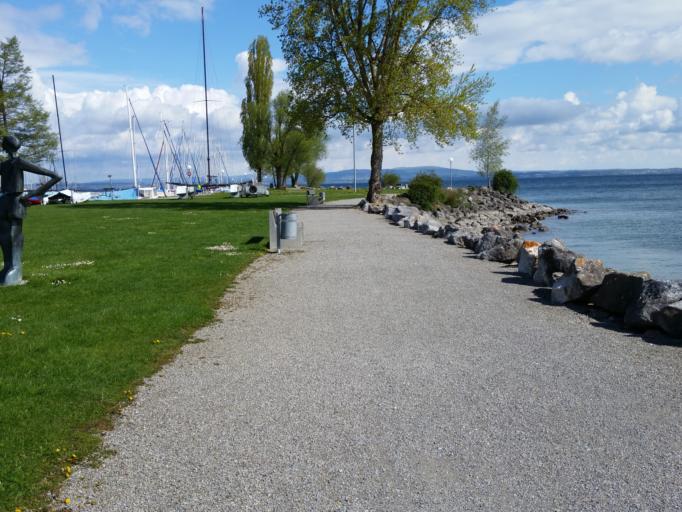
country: CH
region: Thurgau
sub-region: Arbon District
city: Romanshorn
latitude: 47.5678
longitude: 9.3851
